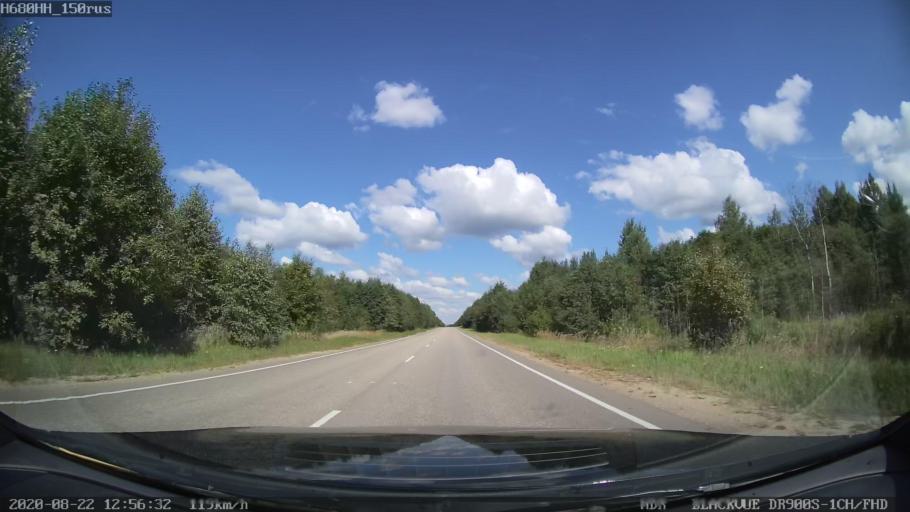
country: RU
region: Tverskaya
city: Rameshki
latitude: 57.5579
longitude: 36.3179
